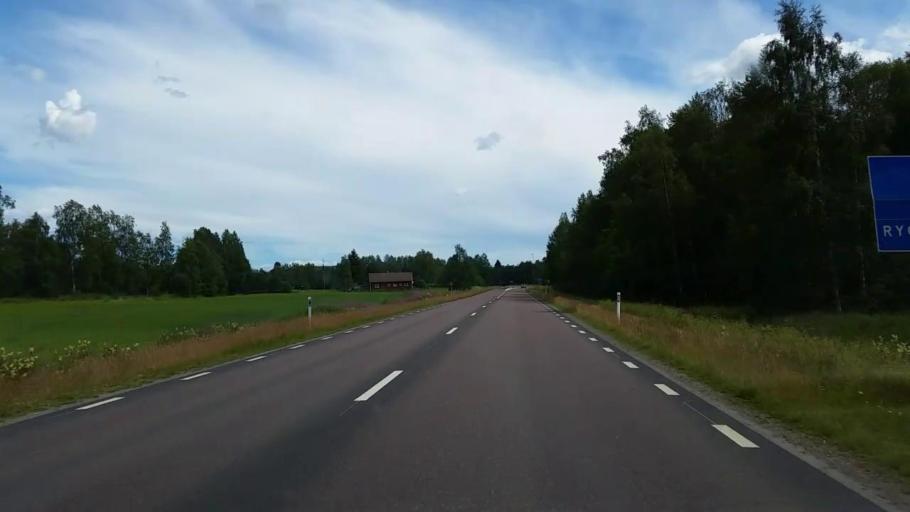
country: SE
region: Gaevleborg
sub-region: Ovanakers Kommun
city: Edsbyn
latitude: 61.3645
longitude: 15.8866
